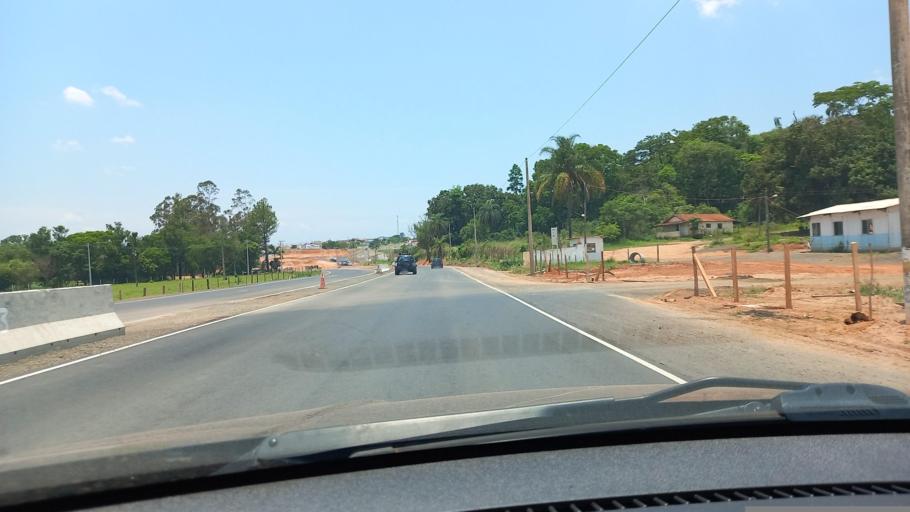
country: BR
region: Sao Paulo
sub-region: Itapira
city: Itapira
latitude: -22.4022
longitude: -46.8464
